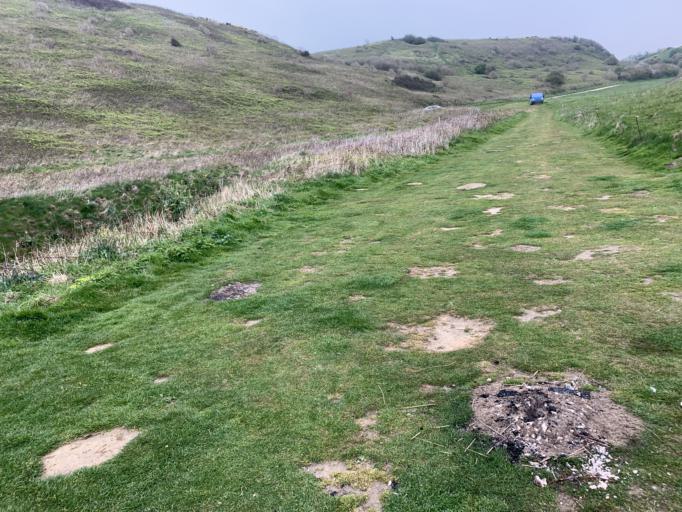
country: FR
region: Haute-Normandie
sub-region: Departement de la Seine-Maritime
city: Etretat
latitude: 49.6885
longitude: 0.1680
